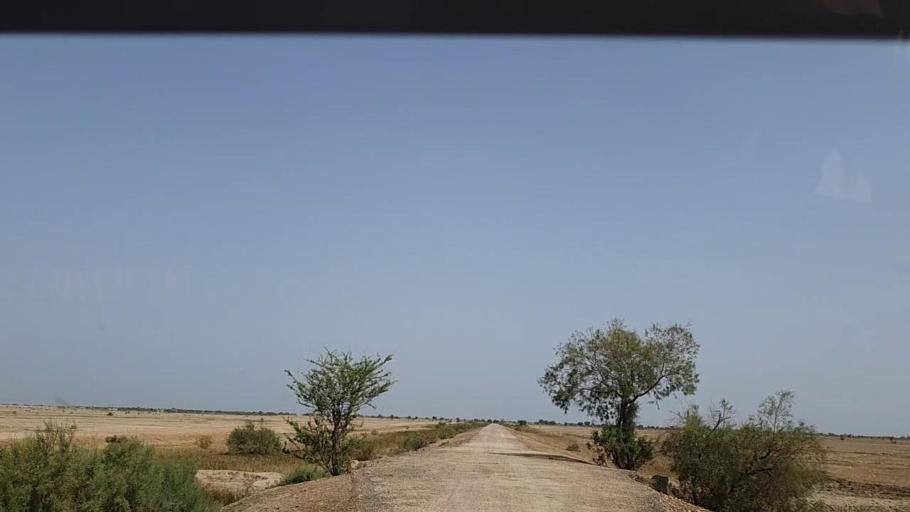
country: PK
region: Sindh
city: Johi
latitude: 26.7654
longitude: 67.6605
